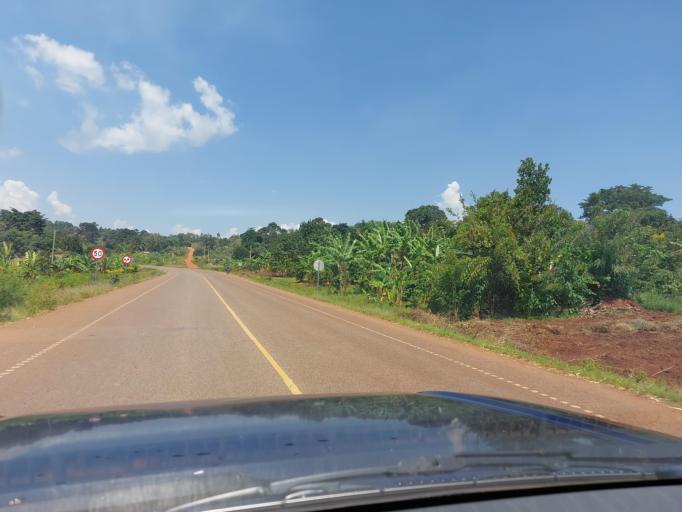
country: UG
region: Central Region
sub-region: Buikwe District
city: Buikwe
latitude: 0.2888
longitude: 33.0882
